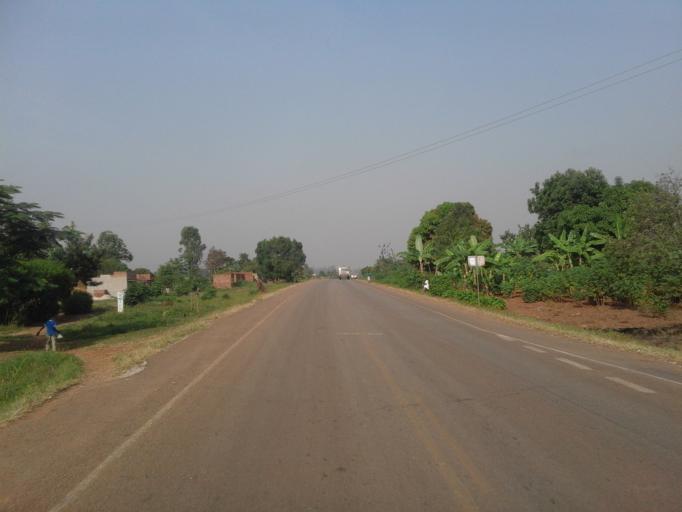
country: UG
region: Eastern Region
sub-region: Mbale District
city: Mbale
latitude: 1.0738
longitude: 34.1185
